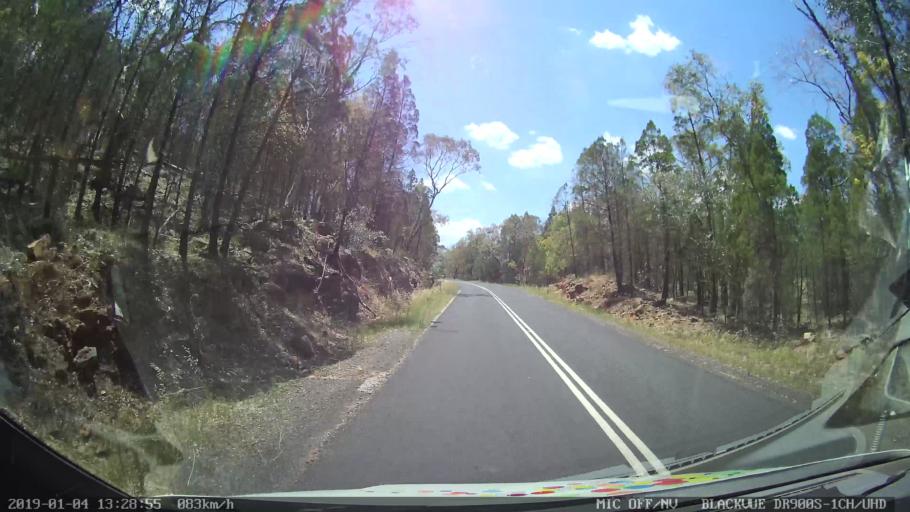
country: AU
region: New South Wales
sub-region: Parkes
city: Peak Hill
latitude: -32.6529
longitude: 148.5499
